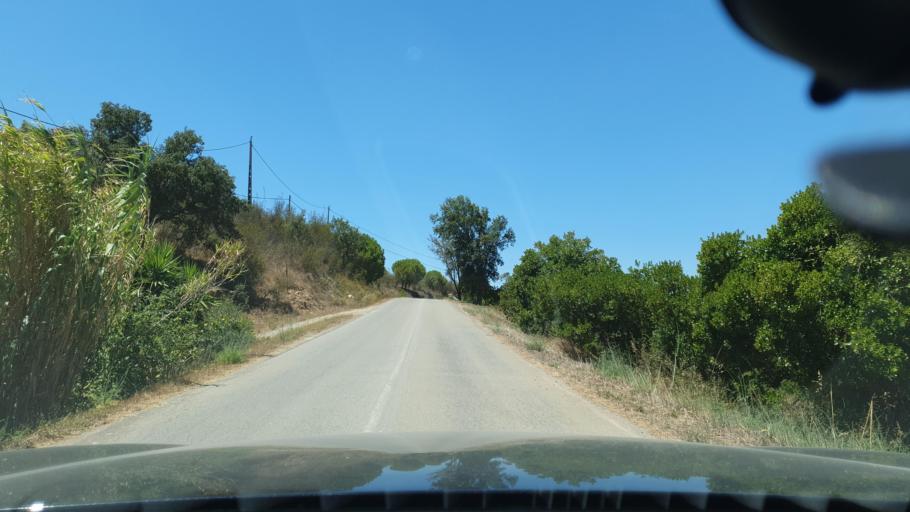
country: PT
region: Beja
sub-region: Odemira
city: Odemira
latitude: 37.5516
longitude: -8.4280
